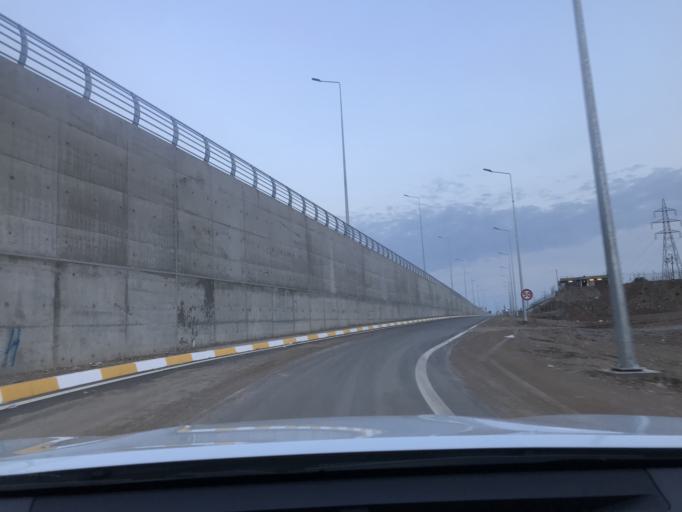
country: IQ
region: Arbil
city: Erbil
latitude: 36.3148
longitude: 43.9107
